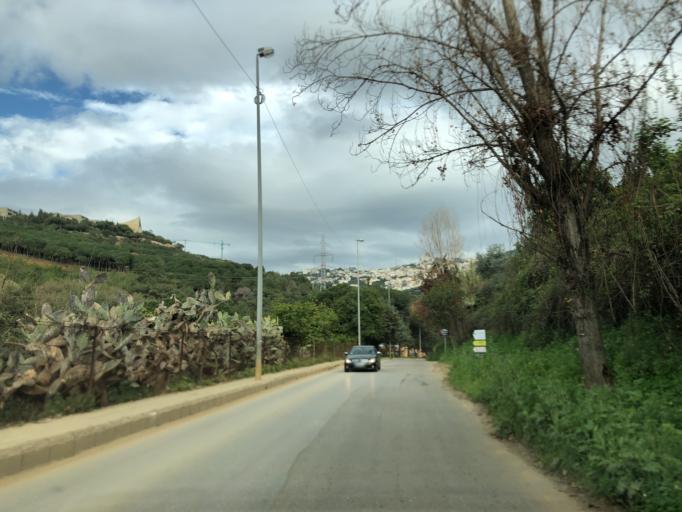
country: LB
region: Mont-Liban
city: Jdaidet el Matn
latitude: 33.8609
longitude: 35.5694
